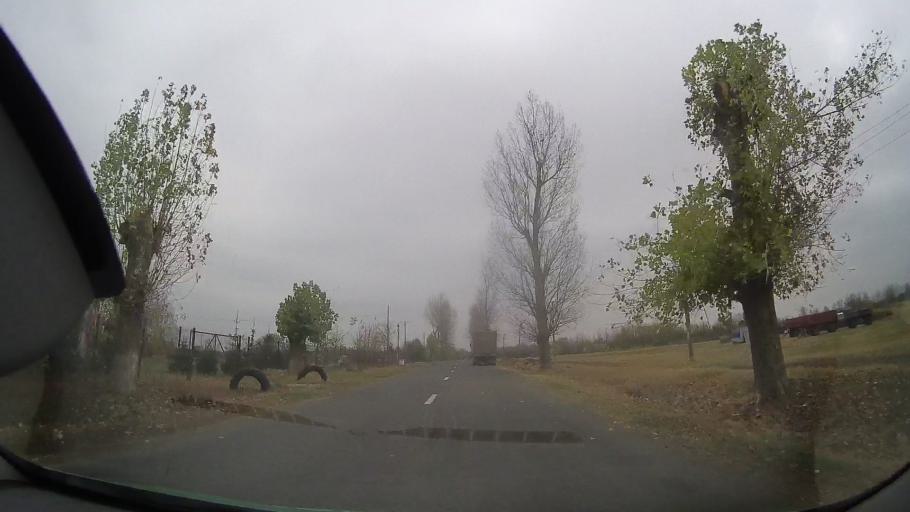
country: RO
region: Ialomita
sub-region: Comuna Grindu
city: Grindu
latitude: 44.7820
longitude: 26.9054
